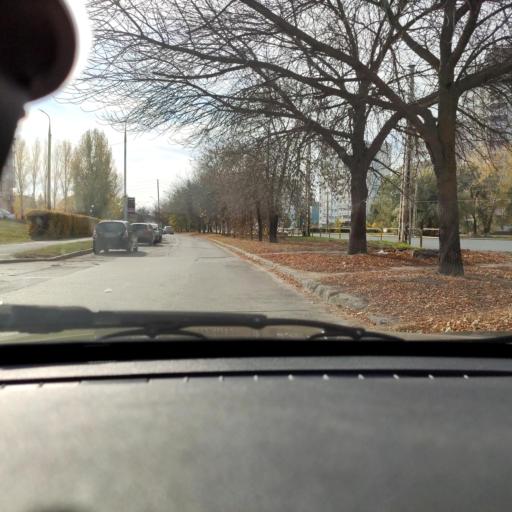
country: RU
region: Samara
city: Tol'yatti
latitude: 53.5050
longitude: 49.3005
